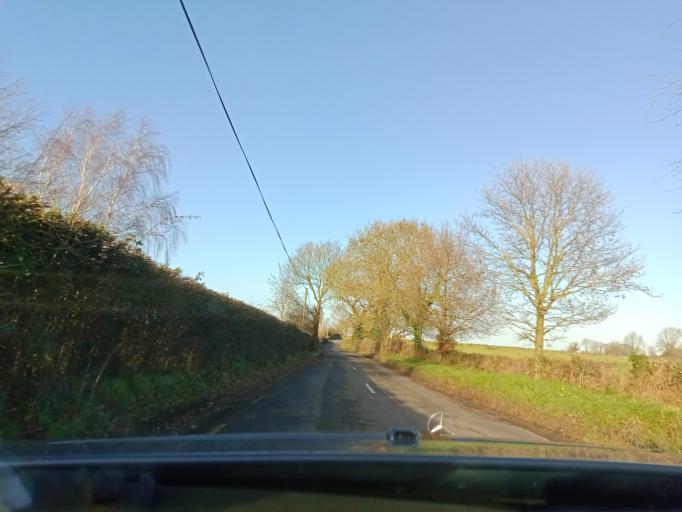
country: IE
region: Leinster
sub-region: Kilkenny
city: Callan
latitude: 52.5062
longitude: -7.3836
